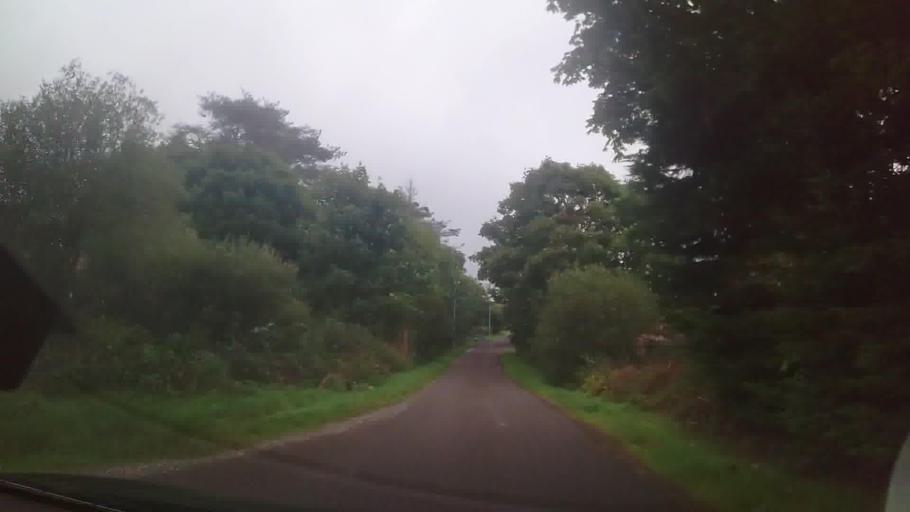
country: GB
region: Scotland
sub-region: Argyll and Bute
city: Isle Of Mull
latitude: 56.6975
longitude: -6.1026
